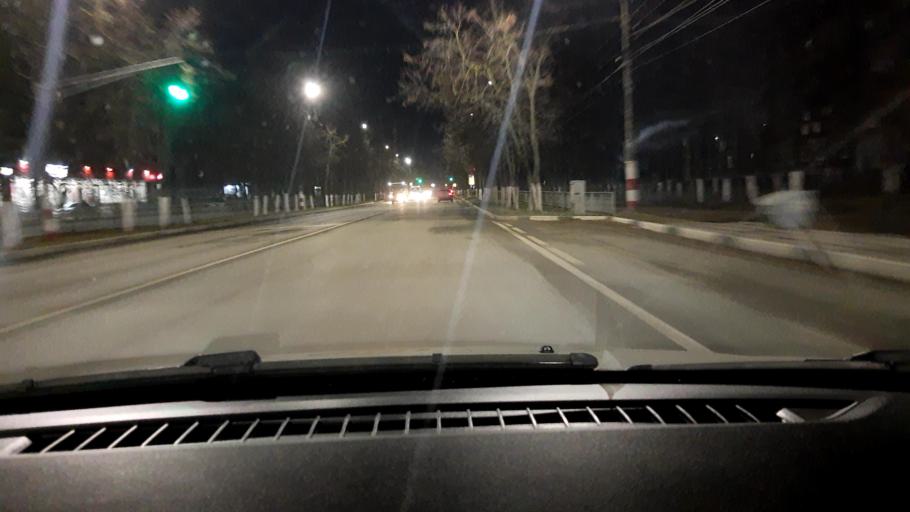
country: RU
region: Nizjnij Novgorod
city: Dzerzhinsk
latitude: 56.2530
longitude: 43.4659
